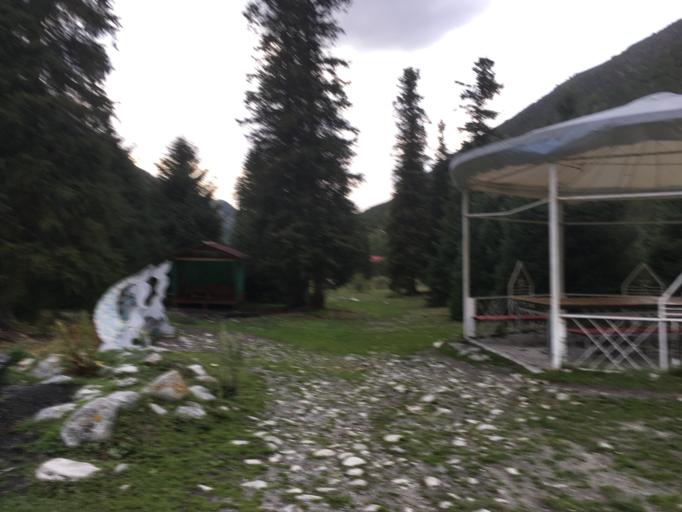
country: KG
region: Chuy
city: Bishkek
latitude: 42.5627
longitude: 74.4826
